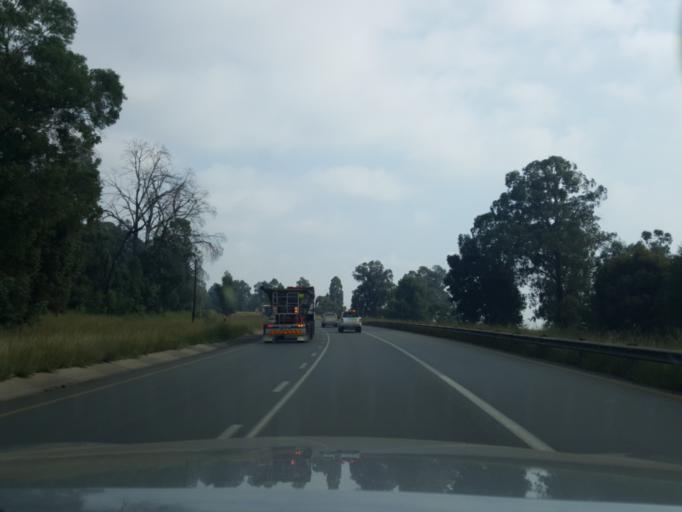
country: ZA
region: Mpumalanga
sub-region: Nkangala District Municipality
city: Witbank
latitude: -25.9922
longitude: 29.2904
